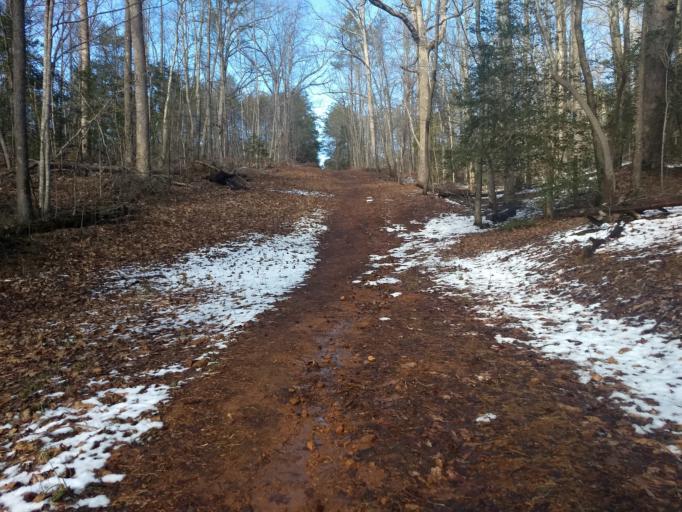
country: US
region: South Carolina
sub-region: Greenville County
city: Wade Hampton
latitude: 34.9283
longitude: -82.3728
